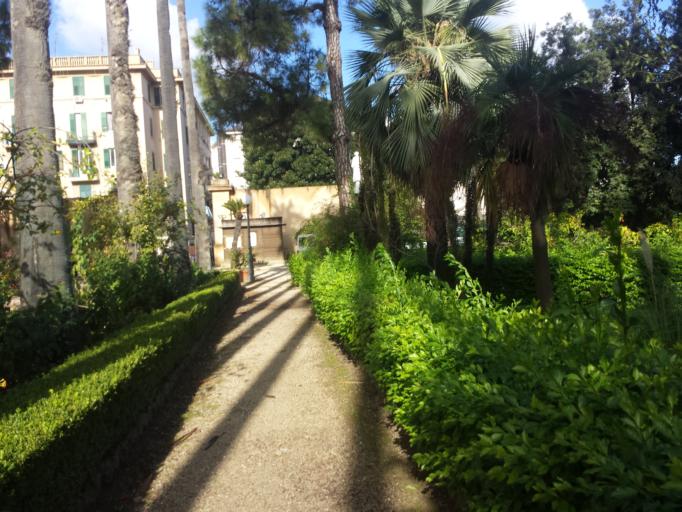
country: IT
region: Sicily
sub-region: Palermo
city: Palermo
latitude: 38.1141
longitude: 13.3752
